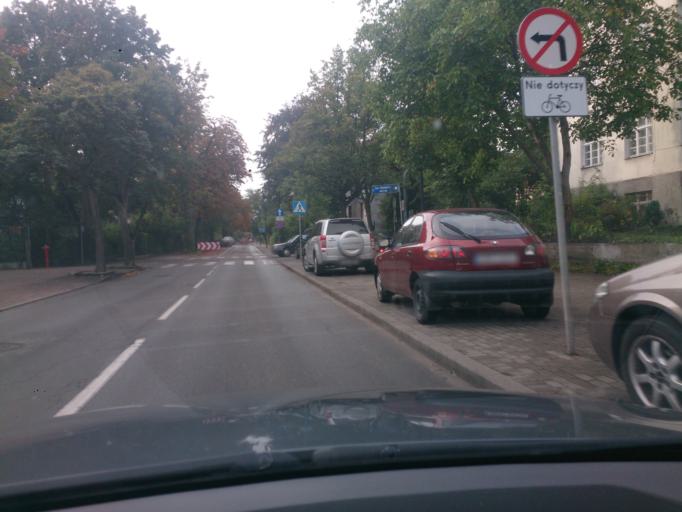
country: PL
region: Pomeranian Voivodeship
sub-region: Sopot
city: Sopot
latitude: 54.4411
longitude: 18.5568
